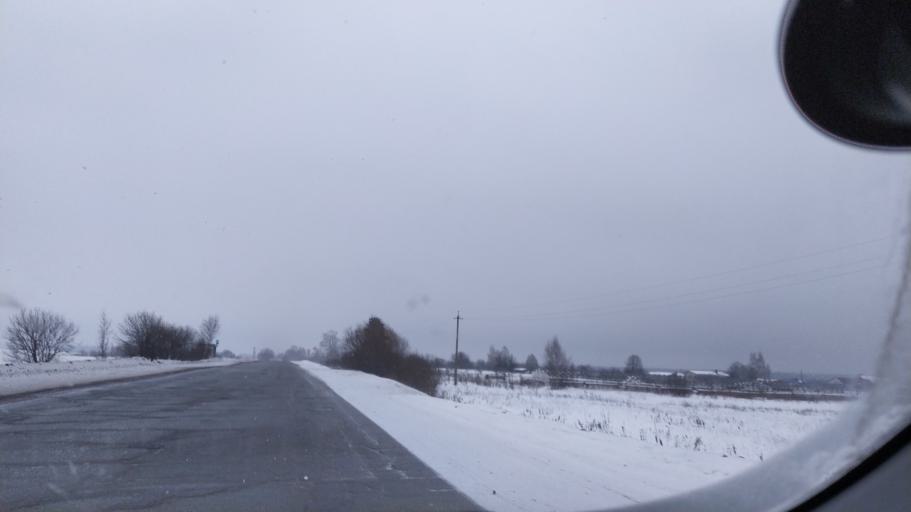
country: RU
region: Mariy-El
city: Krasnogorskiy
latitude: 56.1471
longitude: 48.1291
